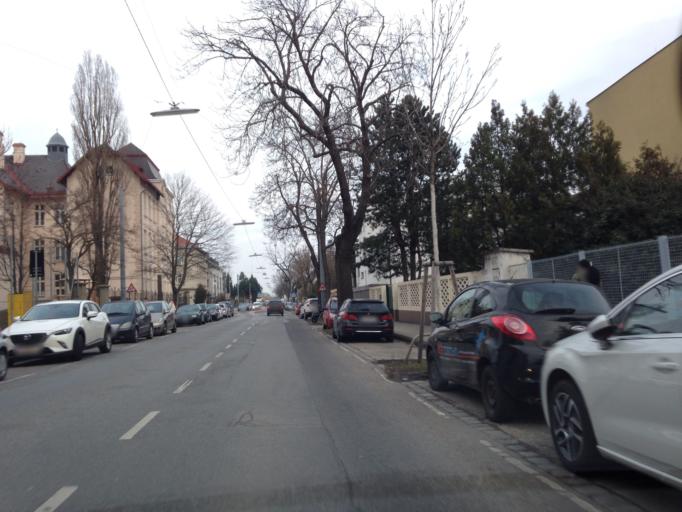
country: AT
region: Lower Austria
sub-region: Politischer Bezirk Wien-Umgebung
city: Gerasdorf bei Wien
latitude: 48.2509
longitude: 16.4452
